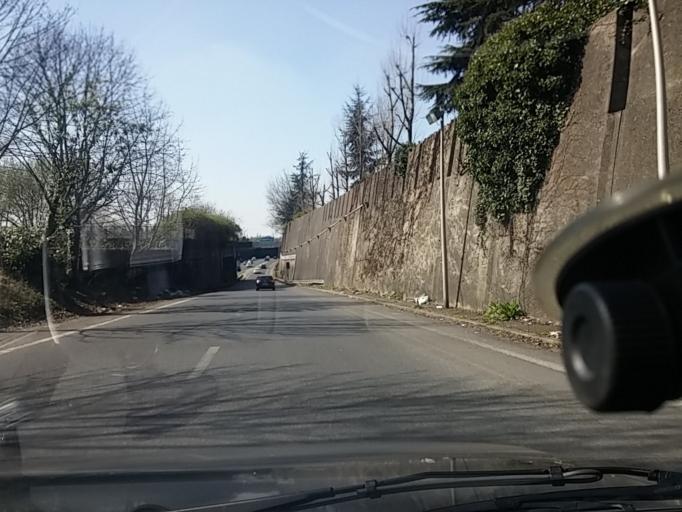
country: FR
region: Ile-de-France
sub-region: Departement du Val-de-Marne
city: Champigny-sur-Marne
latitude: 48.8276
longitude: 2.5085
